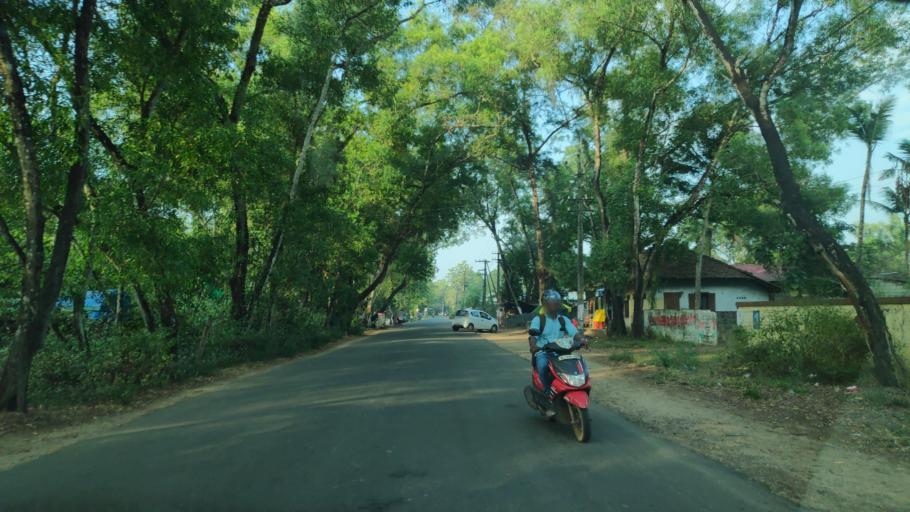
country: IN
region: Kerala
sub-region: Alappuzha
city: Shertallai
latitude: 9.6101
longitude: 76.3617
